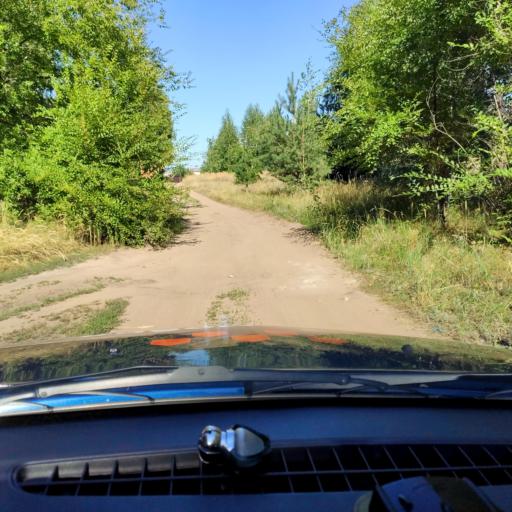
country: RU
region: Voronezj
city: Maslovka
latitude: 51.5436
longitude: 39.1697
